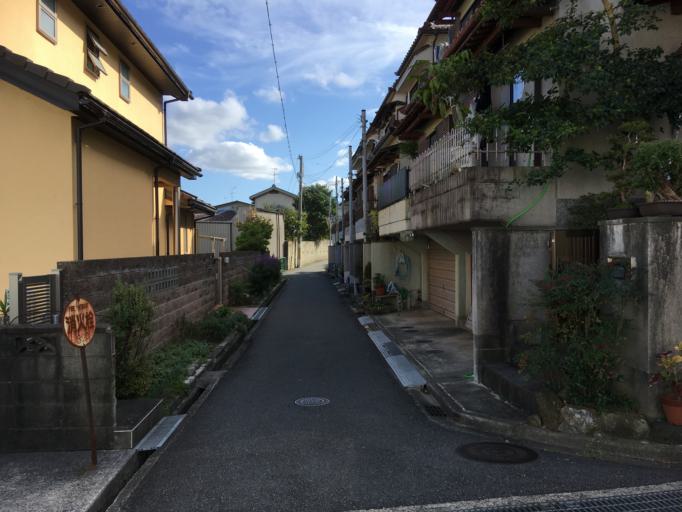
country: JP
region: Nara
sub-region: Ikoma-shi
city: Ikoma
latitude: 34.6726
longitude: 135.7061
